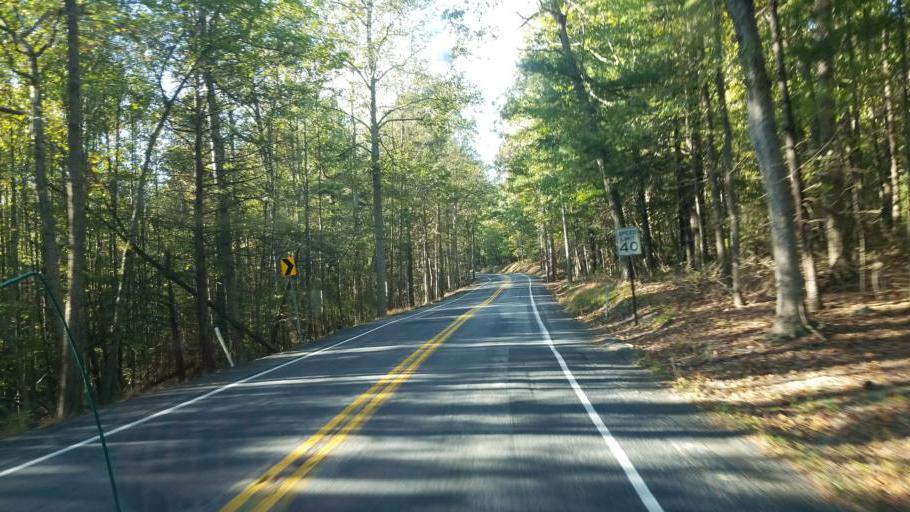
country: US
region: Pennsylvania
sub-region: Franklin County
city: Mont Alto
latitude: 39.8687
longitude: -77.4973
